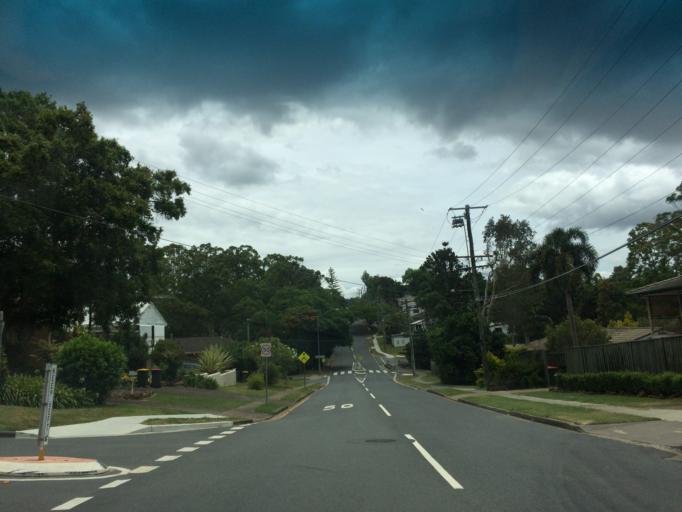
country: AU
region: Queensland
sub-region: Brisbane
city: Kenmore Hills
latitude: -27.5185
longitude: 152.9460
